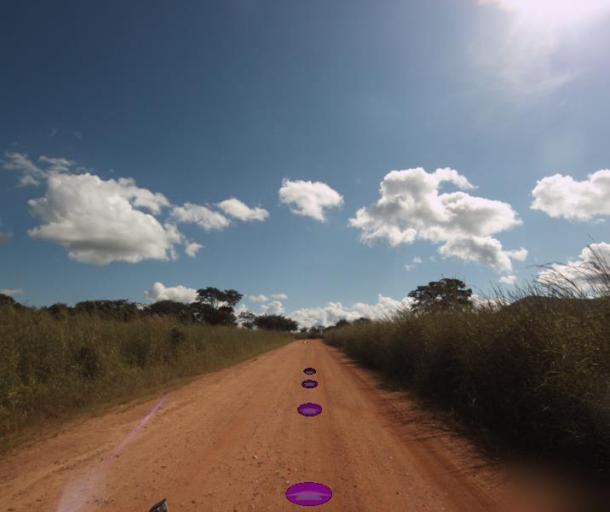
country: BR
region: Goias
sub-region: Jaragua
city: Jaragua
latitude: -15.8361
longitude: -49.2730
